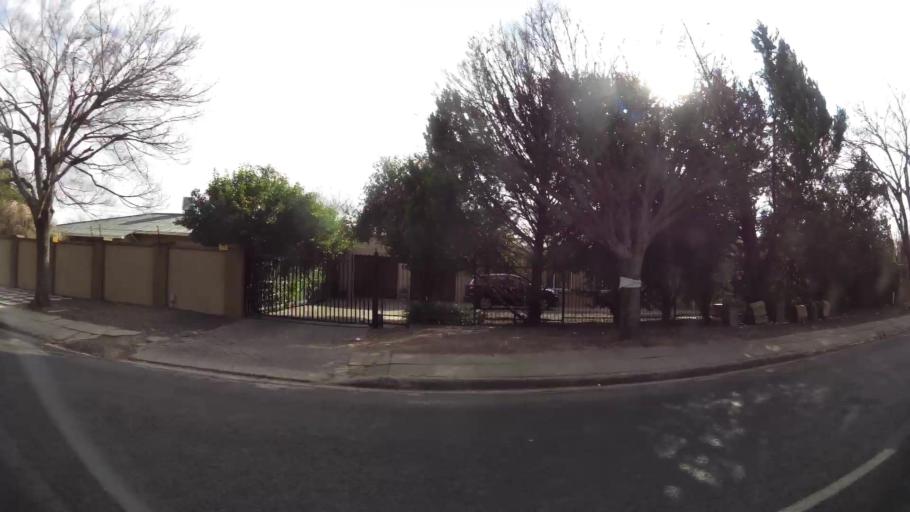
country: ZA
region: Orange Free State
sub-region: Mangaung Metropolitan Municipality
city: Bloemfontein
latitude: -29.0842
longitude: 26.2131
